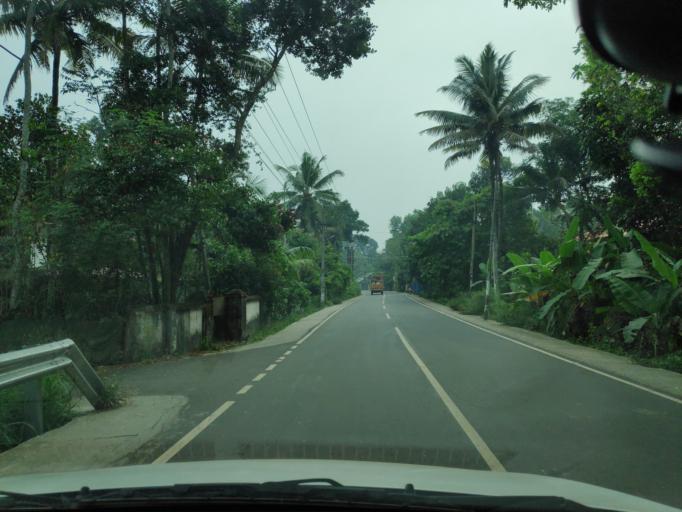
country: IN
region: Kerala
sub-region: Alappuzha
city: Shertallai
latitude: 9.6083
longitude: 76.3419
